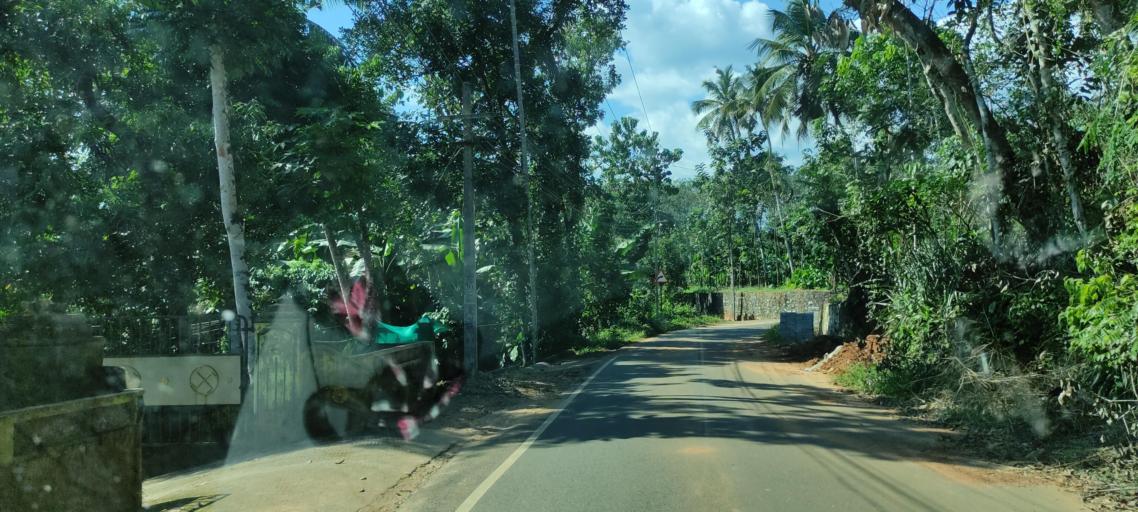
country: IN
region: Kerala
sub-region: Pattanamtitta
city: Adur
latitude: 9.2009
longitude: 76.7489
